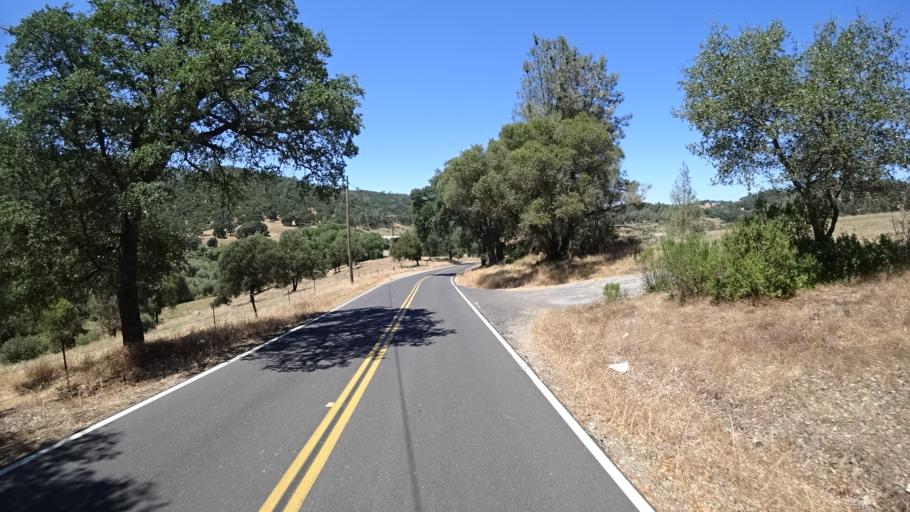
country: US
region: California
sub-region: Calaveras County
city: San Andreas
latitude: 38.1604
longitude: -120.6724
